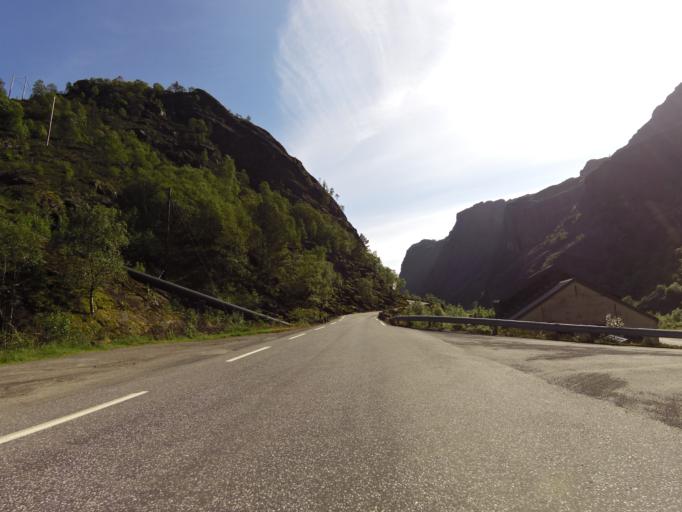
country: NO
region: Rogaland
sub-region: Sokndal
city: Hauge i Dalane
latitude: 58.3292
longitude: 6.3562
